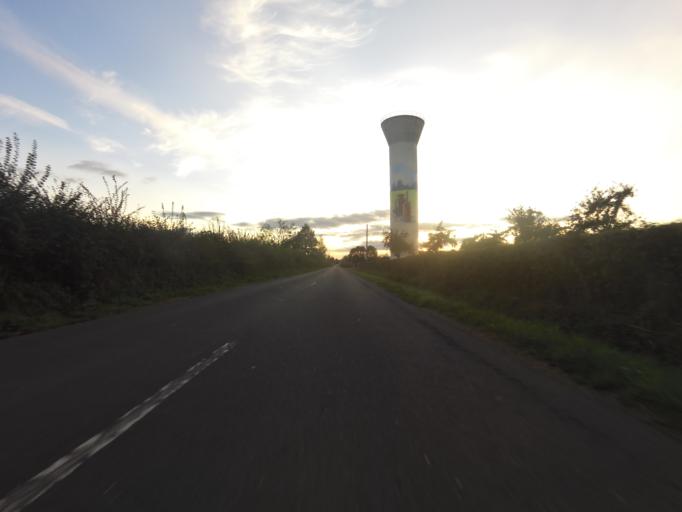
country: FR
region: Lower Normandy
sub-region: Departement du Calvados
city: La Vespiere
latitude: 48.9786
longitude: 0.3397
